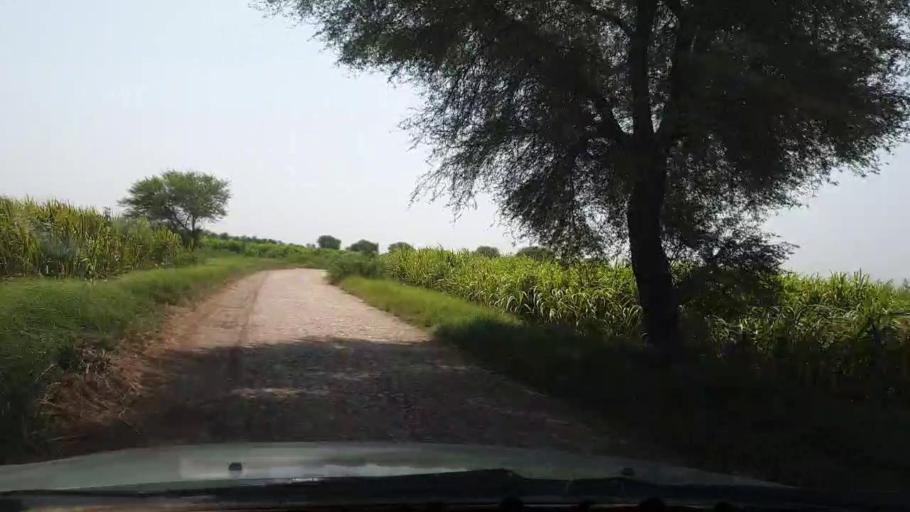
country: PK
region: Sindh
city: Tando Muhammad Khan
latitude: 25.1992
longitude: 68.6658
